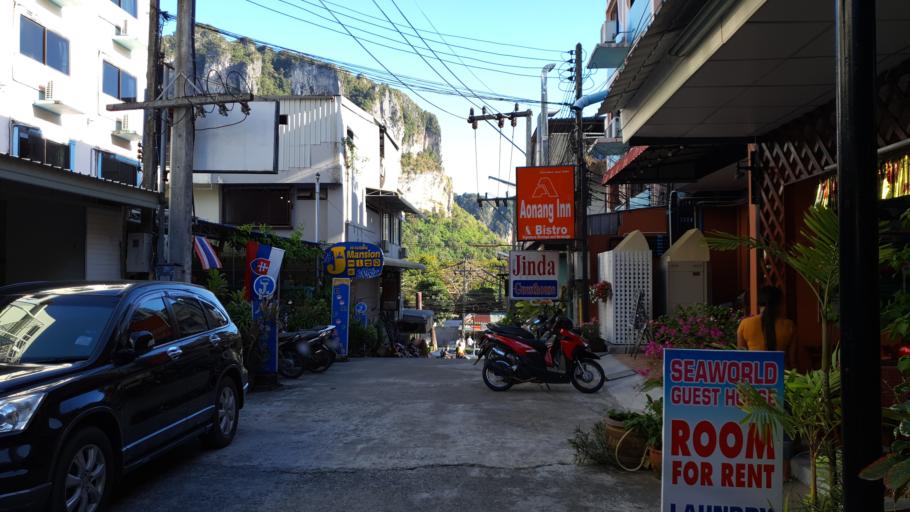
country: TH
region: Phangnga
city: Ban Ao Nang
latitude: 8.0326
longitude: 98.8228
